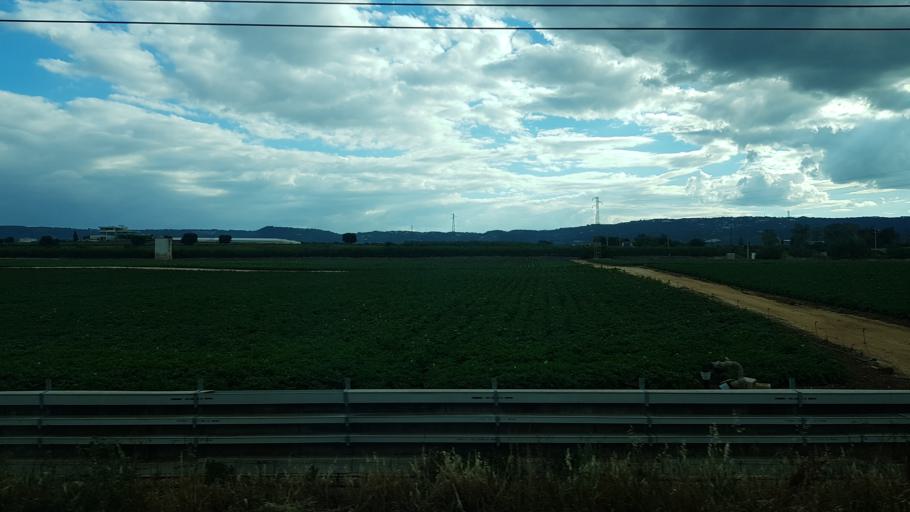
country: IT
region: Apulia
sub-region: Provincia di Brindisi
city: Fasano
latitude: 40.8483
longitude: 17.3907
